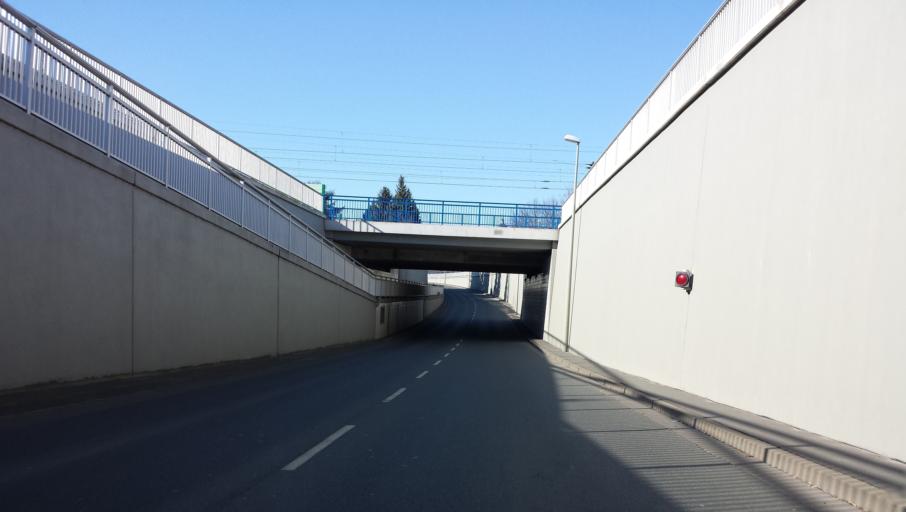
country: DE
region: Hesse
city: Gernsheim
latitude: 49.7517
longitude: 8.4915
